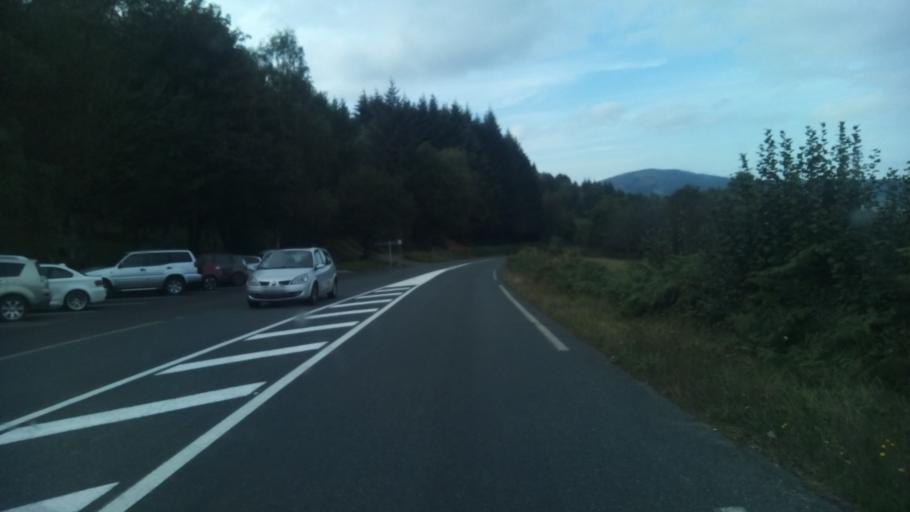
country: FR
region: Rhone-Alpes
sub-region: Departement du Rhone
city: Beaujeu
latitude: 46.2076
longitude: 4.5354
